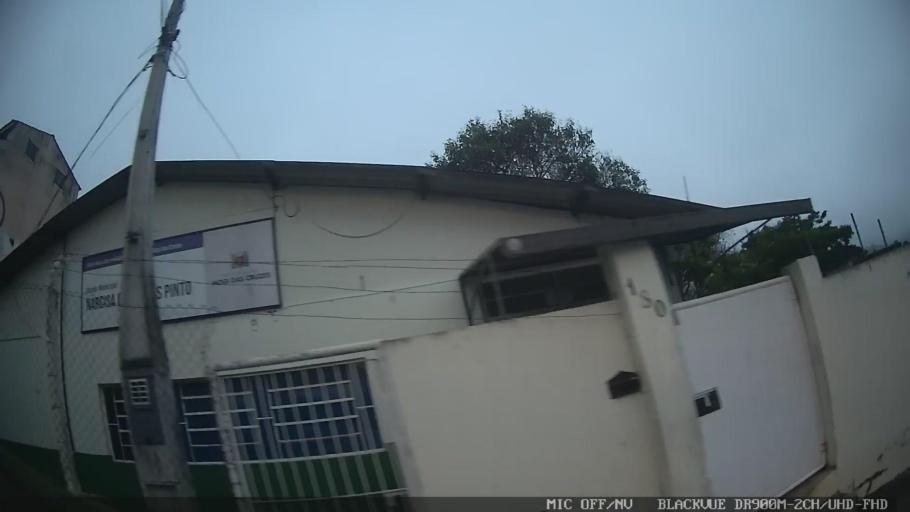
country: BR
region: Sao Paulo
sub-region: Mogi das Cruzes
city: Mogi das Cruzes
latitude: -23.5042
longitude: -46.2157
